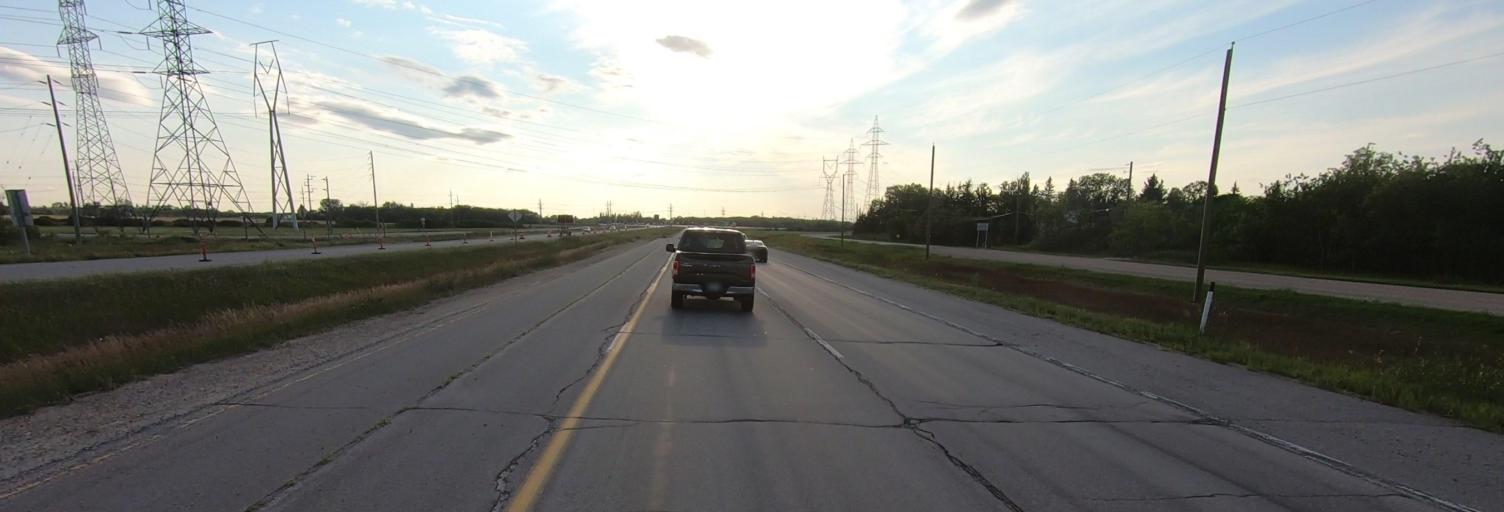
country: CA
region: Manitoba
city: Winnipeg
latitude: 49.9670
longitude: -97.0002
